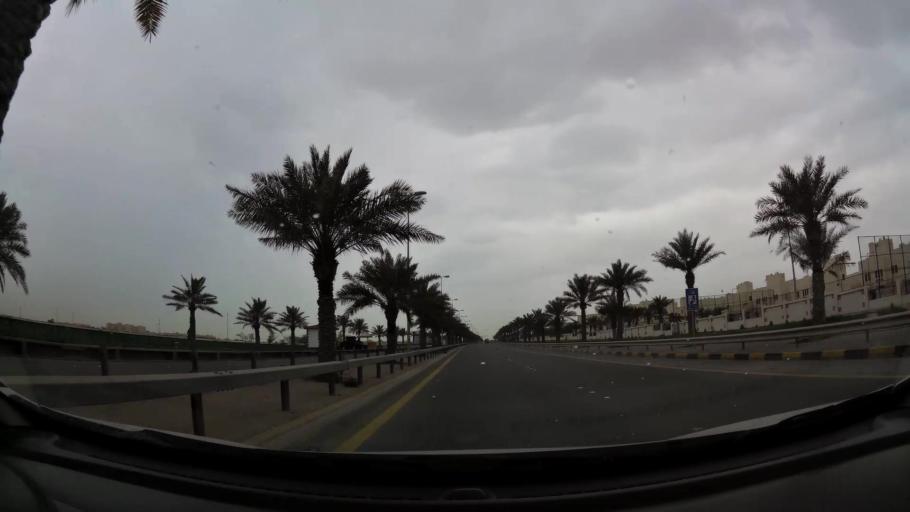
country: BH
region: Northern
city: Ar Rifa'
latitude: 26.1060
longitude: 50.5405
